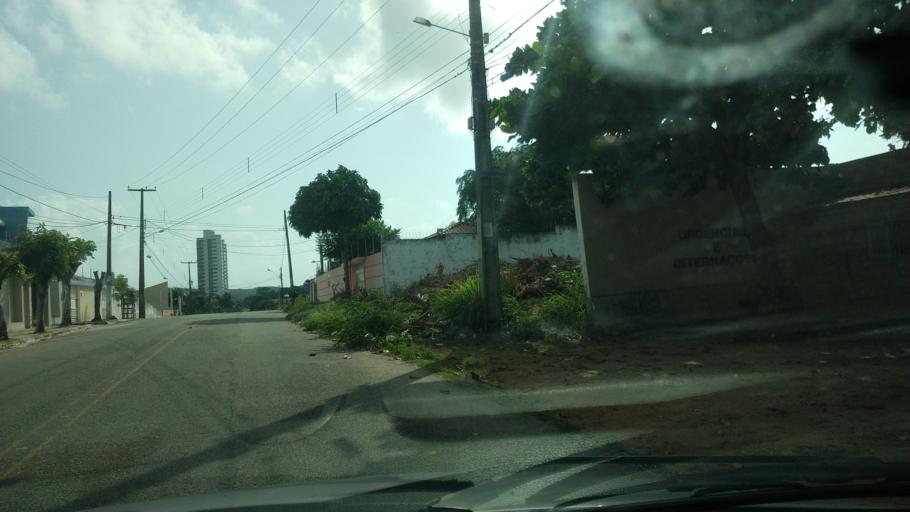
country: BR
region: Rio Grande do Norte
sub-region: Natal
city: Natal
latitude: -5.8603
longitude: -35.2043
